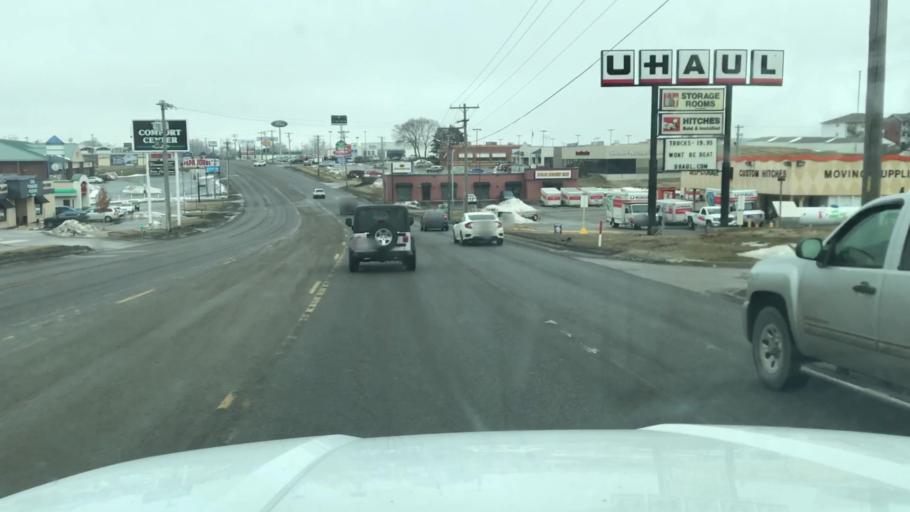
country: US
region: Missouri
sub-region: Buchanan County
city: Saint Joseph
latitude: 39.7819
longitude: -94.8030
